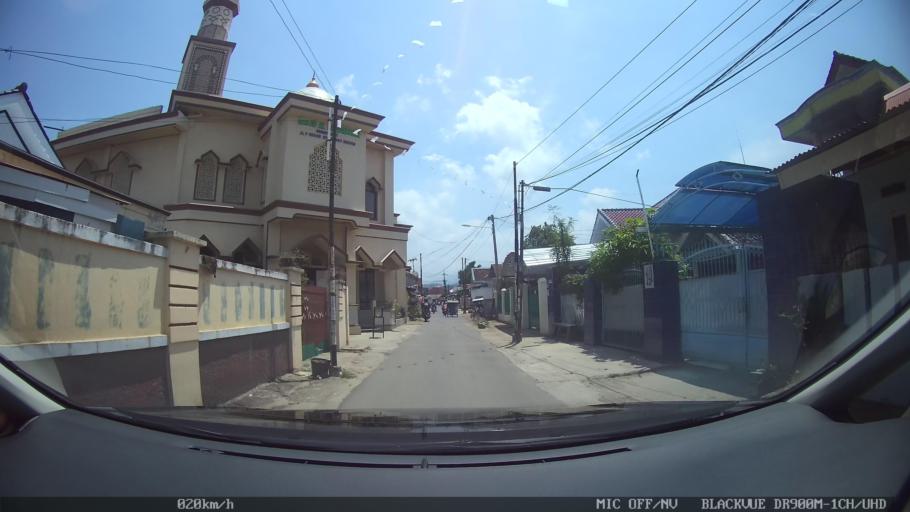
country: ID
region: Lampung
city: Bandarlampung
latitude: -5.4058
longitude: 105.2673
